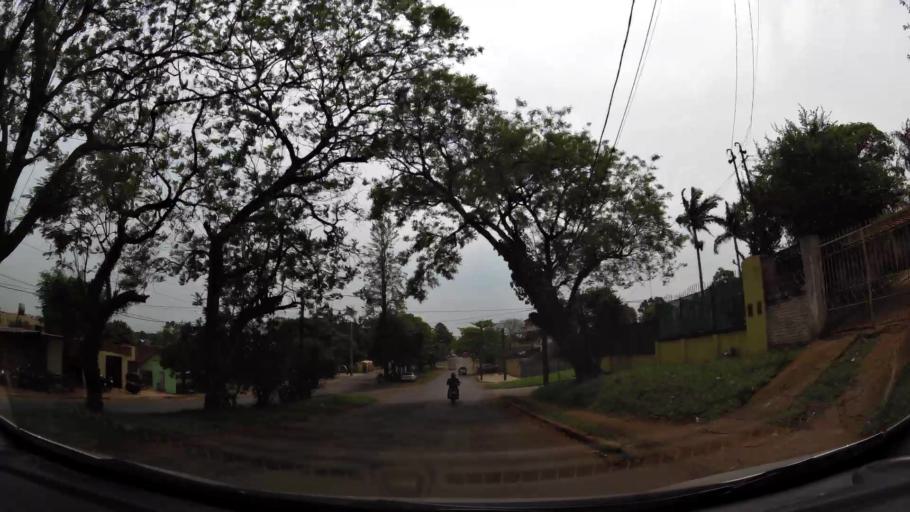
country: PY
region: Alto Parana
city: Presidente Franco
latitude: -25.5519
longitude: -54.6278
